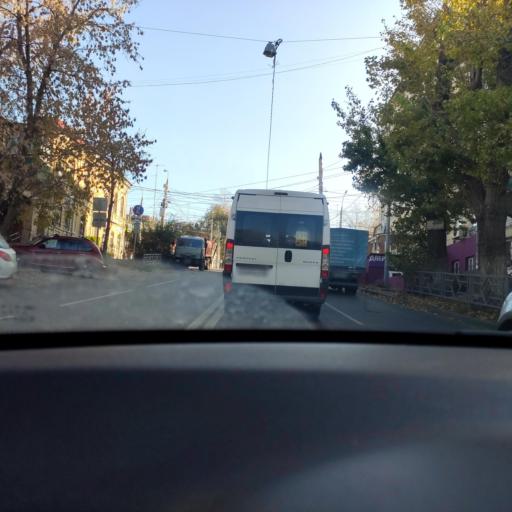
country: RU
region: Samara
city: Rozhdestveno
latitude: 53.1803
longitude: 50.0757
